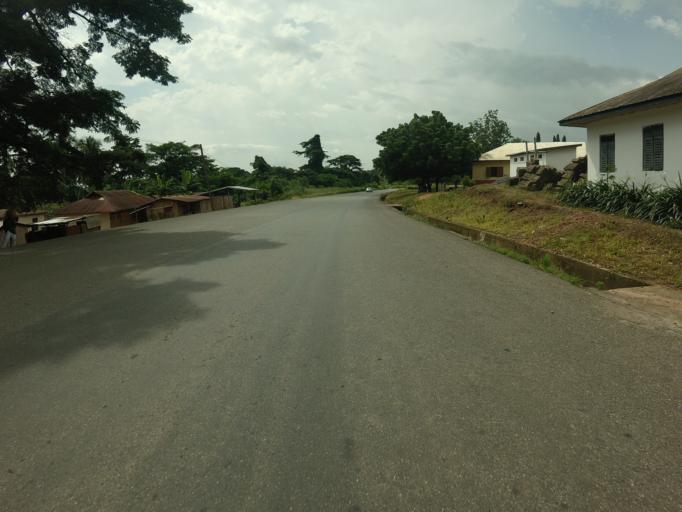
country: GH
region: Volta
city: Kpandu
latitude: 6.8751
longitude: 0.4212
